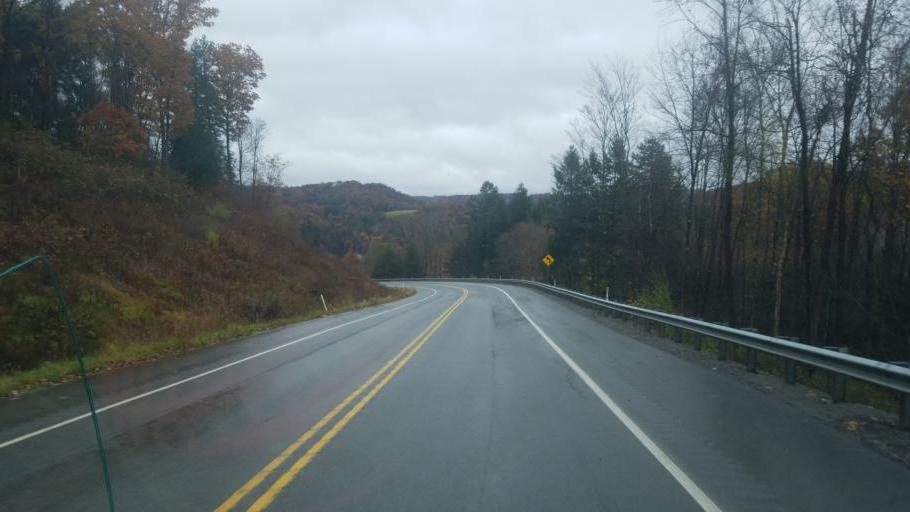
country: US
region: Pennsylvania
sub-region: Clearfield County
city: Clearfield
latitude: 41.0435
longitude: -78.3824
